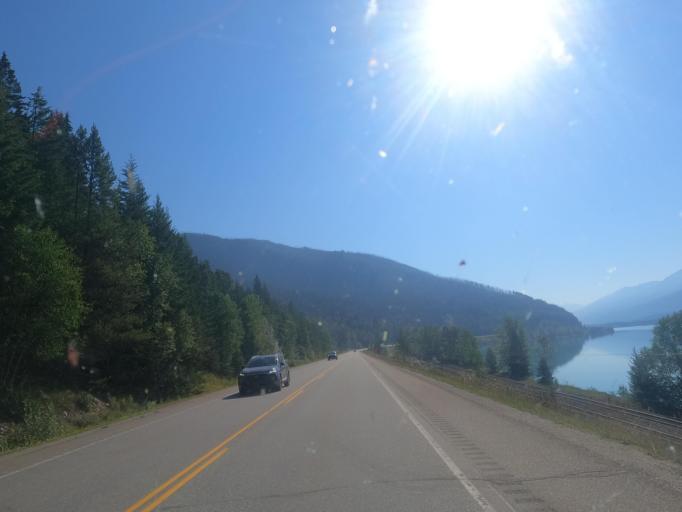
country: CA
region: Alberta
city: Jasper Park Lodge
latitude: 52.9533
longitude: -118.8751
